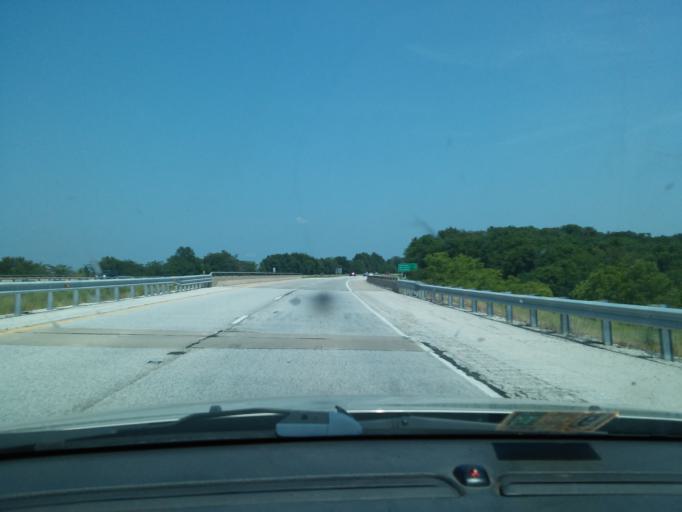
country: US
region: Illinois
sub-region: Morgan County
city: Jacksonville
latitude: 39.7354
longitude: -90.1543
